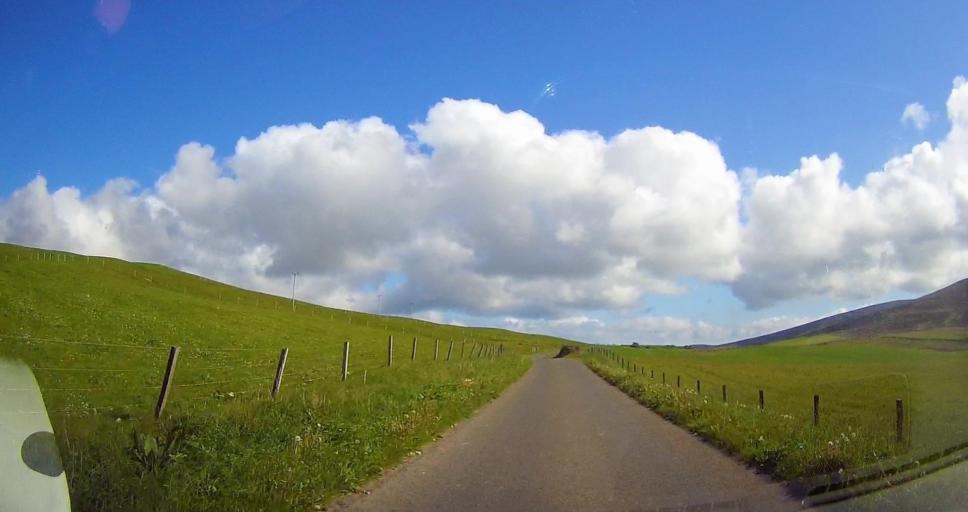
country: GB
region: Scotland
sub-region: Orkney Islands
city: Stromness
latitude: 58.9802
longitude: -3.1368
